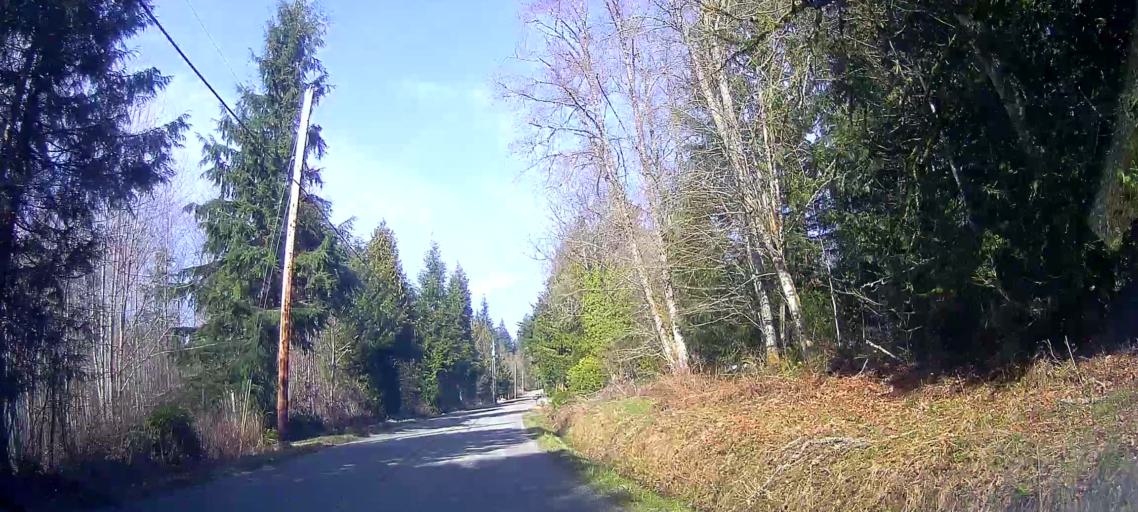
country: US
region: Washington
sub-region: Whatcom County
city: Sudden Valley
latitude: 48.6008
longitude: -122.3664
